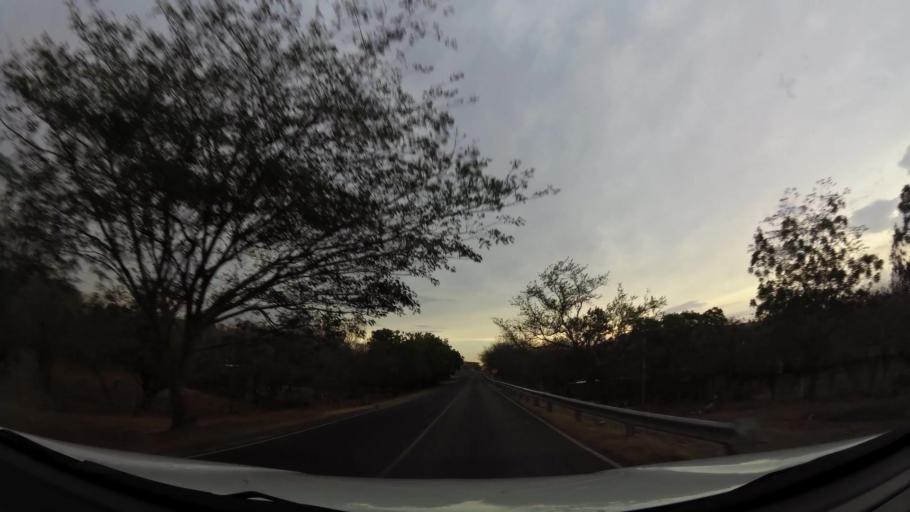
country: NI
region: Leon
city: La Jicaral
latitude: 12.6733
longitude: -86.4293
